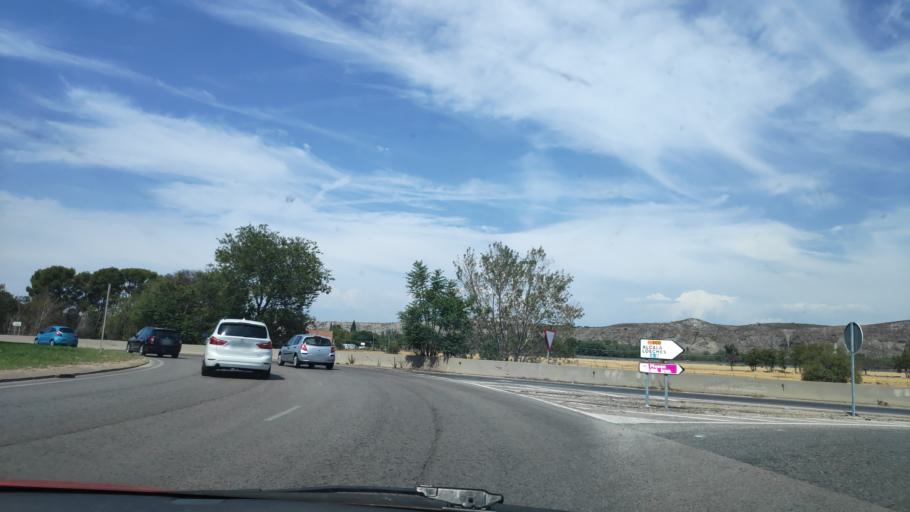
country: ES
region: Madrid
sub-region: Provincia de Madrid
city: Vaciamadrid
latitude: 40.3123
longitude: -3.4885
